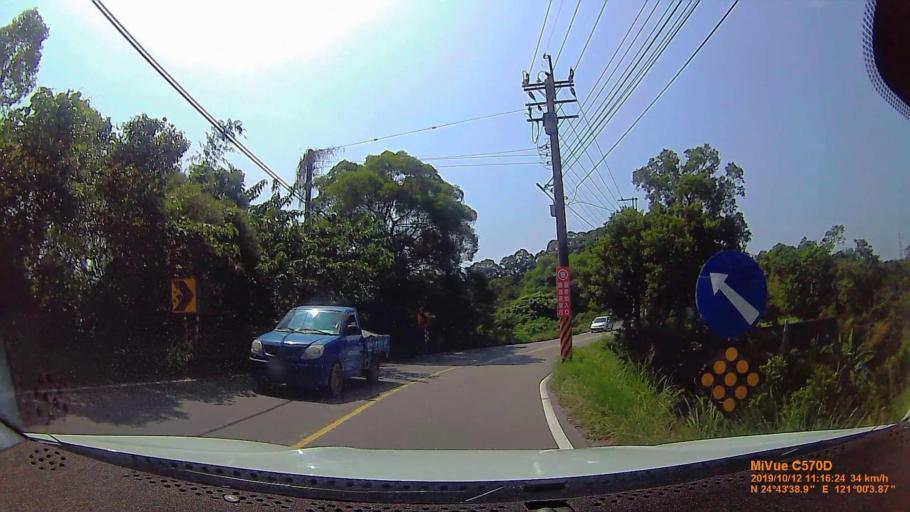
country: TW
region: Taiwan
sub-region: Hsinchu
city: Hsinchu
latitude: 24.7274
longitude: 121.0010
